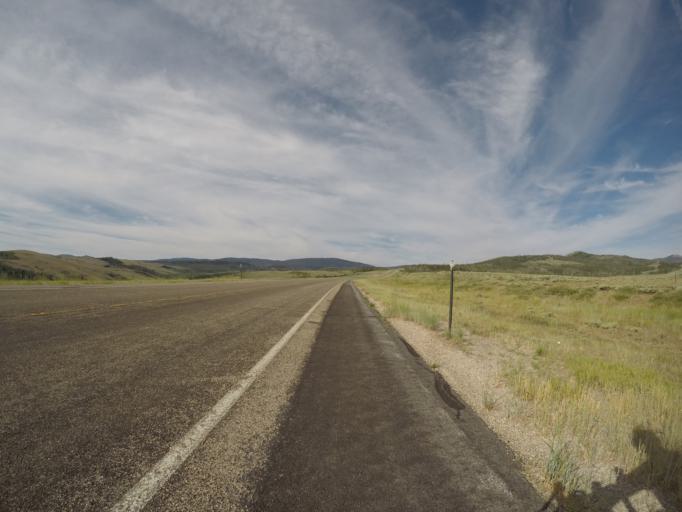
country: US
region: Wyoming
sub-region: Carbon County
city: Saratoga
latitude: 41.1897
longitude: -106.8537
